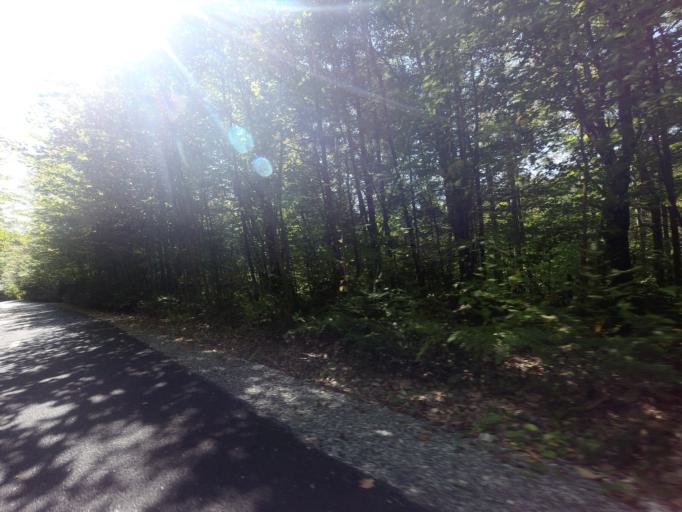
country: CA
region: Quebec
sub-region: Laurentides
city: Mont-Tremblant
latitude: 46.1242
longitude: -74.4990
